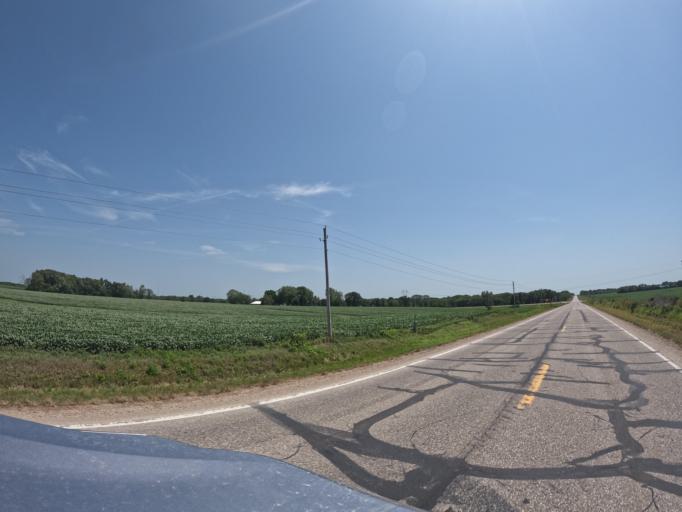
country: US
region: Iowa
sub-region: Henry County
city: Mount Pleasant
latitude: 40.9703
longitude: -91.6124
